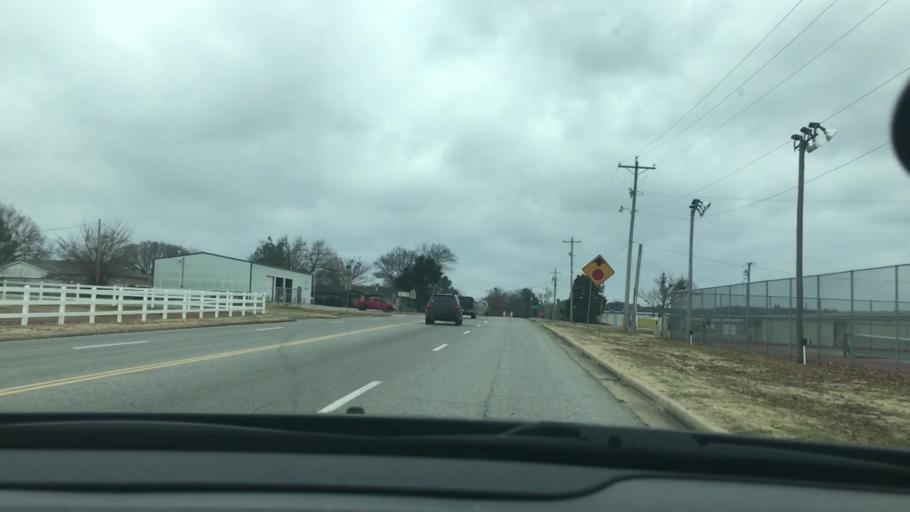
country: US
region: Oklahoma
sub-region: Atoka County
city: Atoka
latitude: 34.3772
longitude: -96.1454
